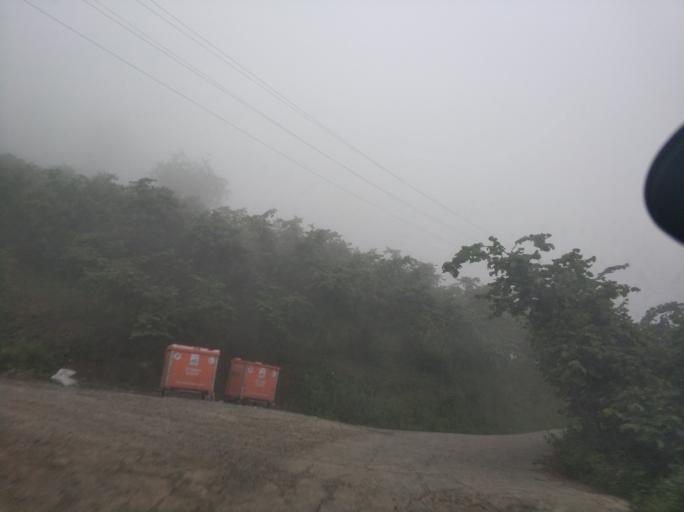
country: TR
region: Giresun
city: Nefsipiraziz
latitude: 40.8867
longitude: 38.0809
